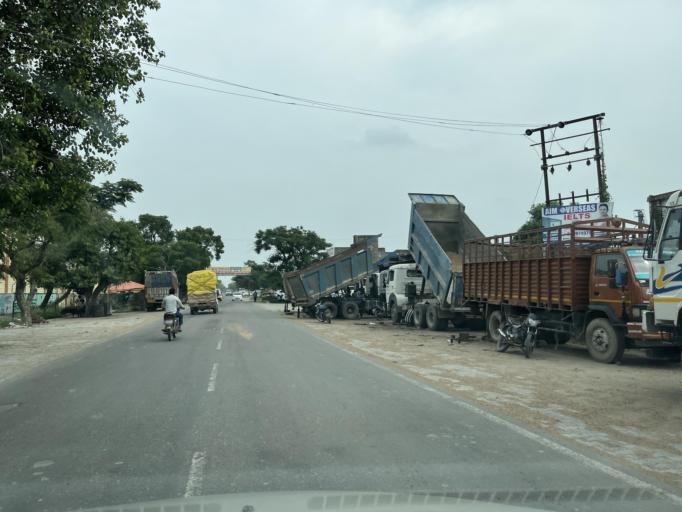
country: IN
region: Uttar Pradesh
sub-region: Rampur
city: Bilaspur
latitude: 29.0377
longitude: 79.2538
